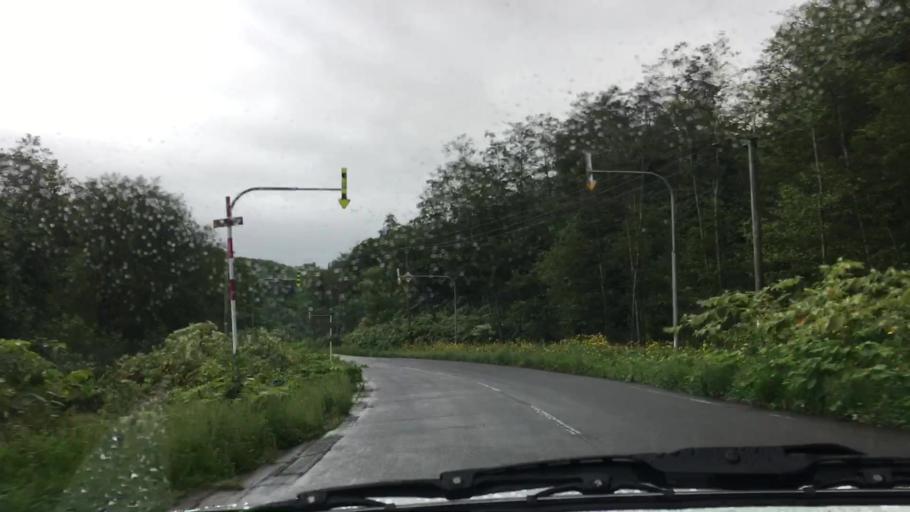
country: JP
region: Hokkaido
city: Niseko Town
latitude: 42.6688
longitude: 140.7773
